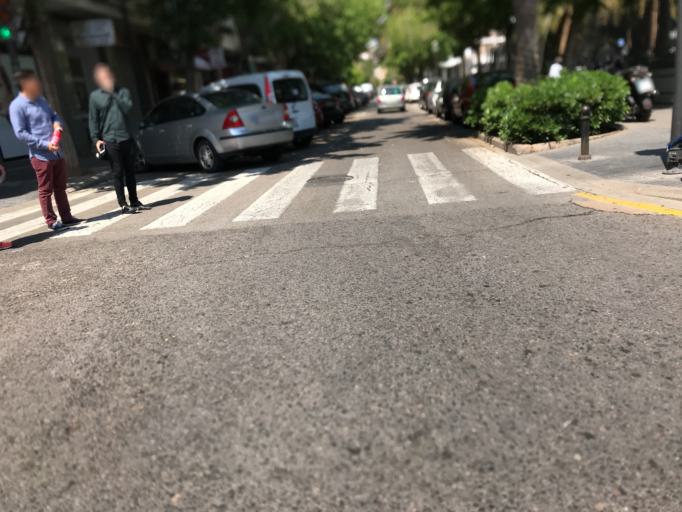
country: ES
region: Valencia
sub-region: Provincia de Valencia
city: Valencia
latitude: 39.4691
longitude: -0.3498
